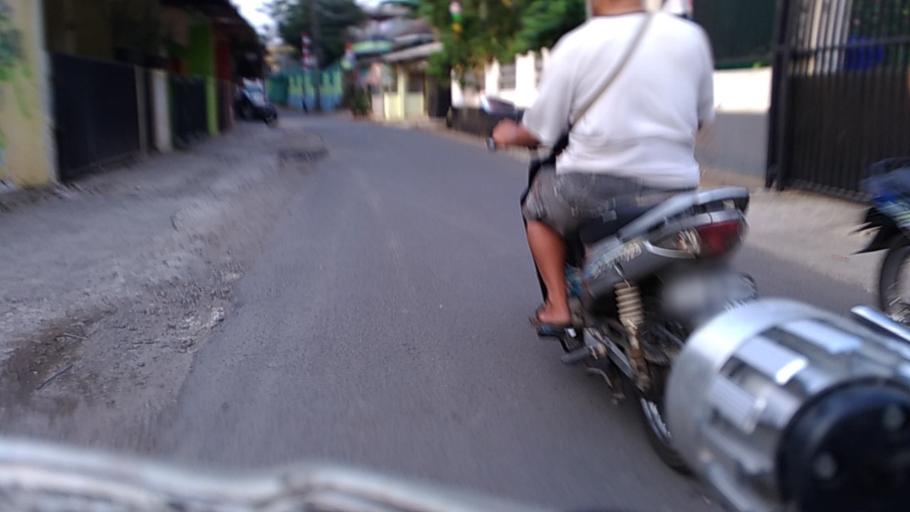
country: ID
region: West Java
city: Depok
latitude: -6.3614
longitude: 106.8806
